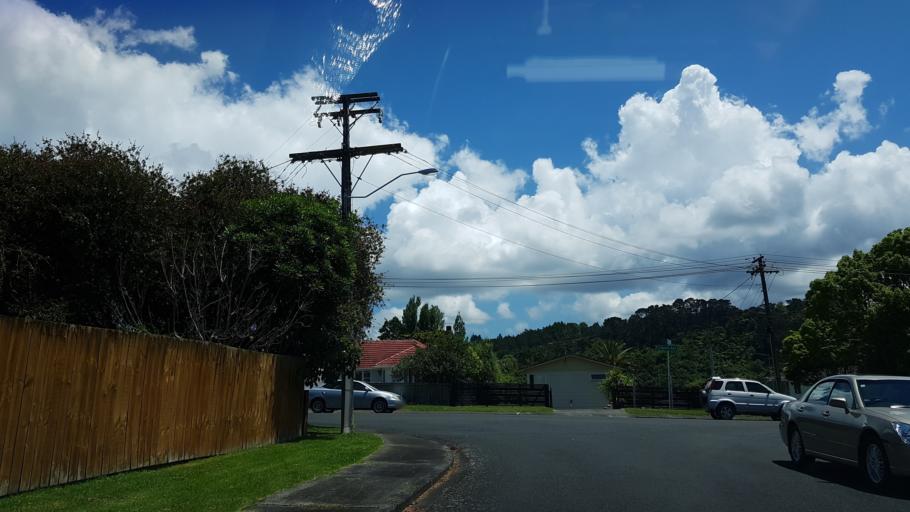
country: NZ
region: Auckland
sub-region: Auckland
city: North Shore
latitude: -36.7849
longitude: 174.6943
